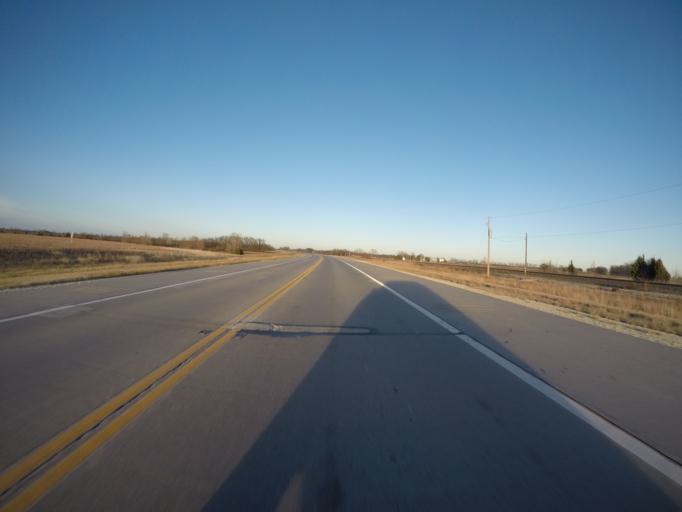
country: US
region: Kansas
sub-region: Harvey County
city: North Newton
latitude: 38.0725
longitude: -97.3017
